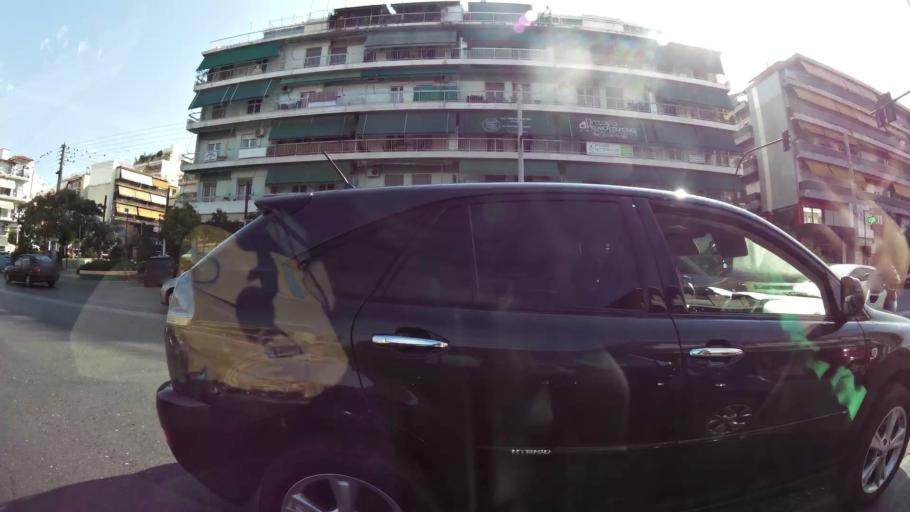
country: GR
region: Attica
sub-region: Nomarchia Athinas
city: Galatsi
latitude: 38.0188
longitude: 23.7559
